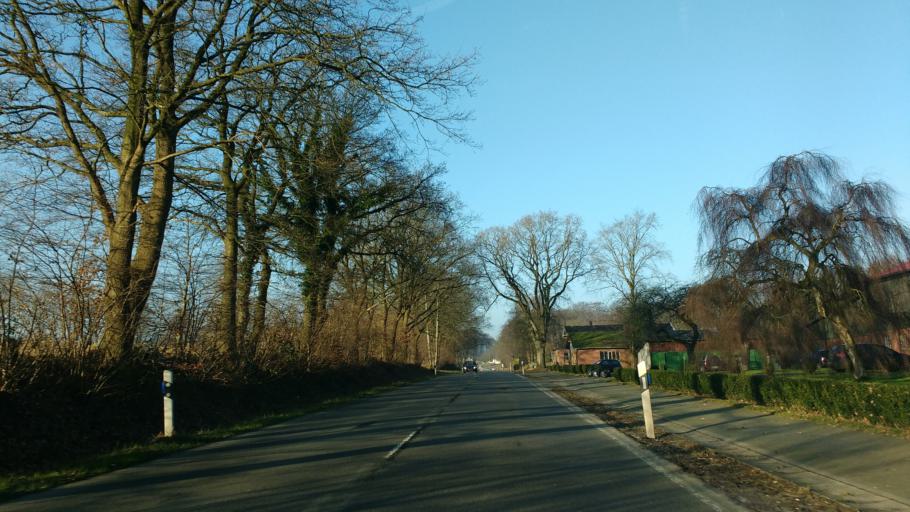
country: DE
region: Schleswig-Holstein
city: Nienbuttel
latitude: 54.0252
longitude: 9.4200
